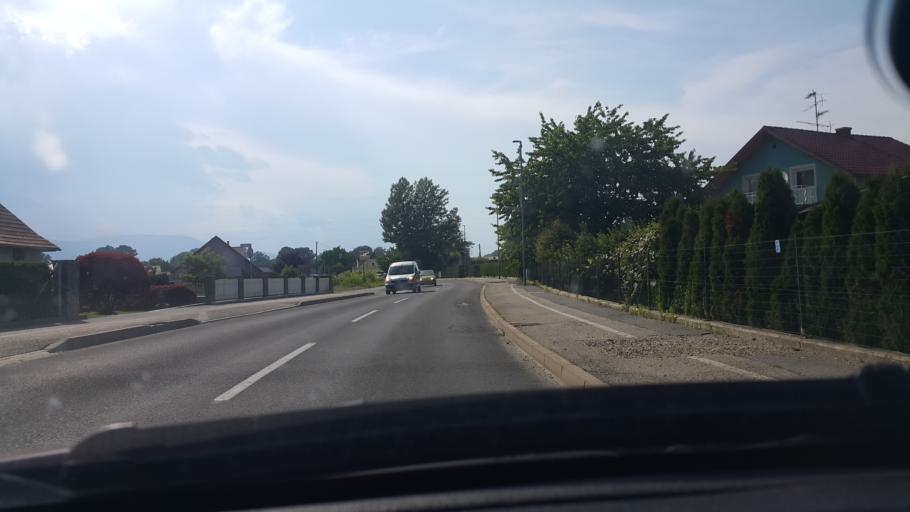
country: SI
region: Duplek
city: Spodnji Duplek
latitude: 46.5031
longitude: 15.7479
